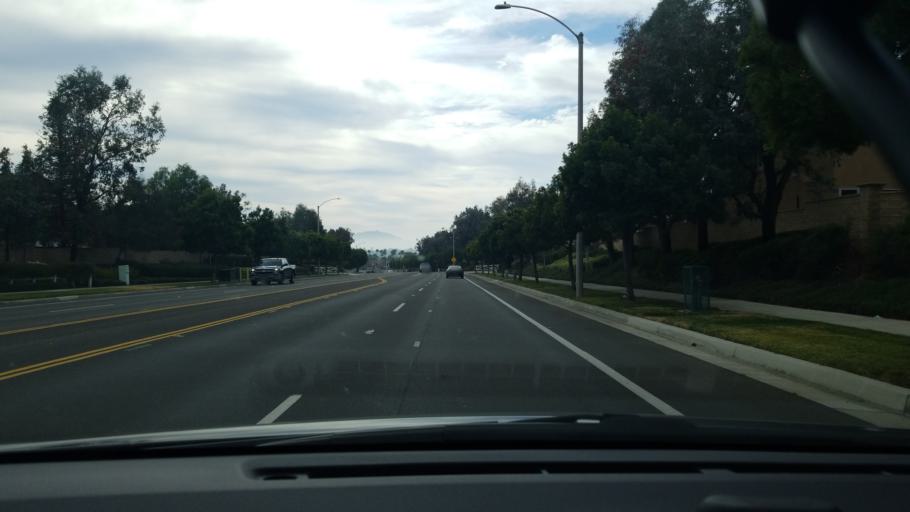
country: US
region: California
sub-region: Riverside County
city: Murrieta Hot Springs
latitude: 33.5575
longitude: -117.1107
